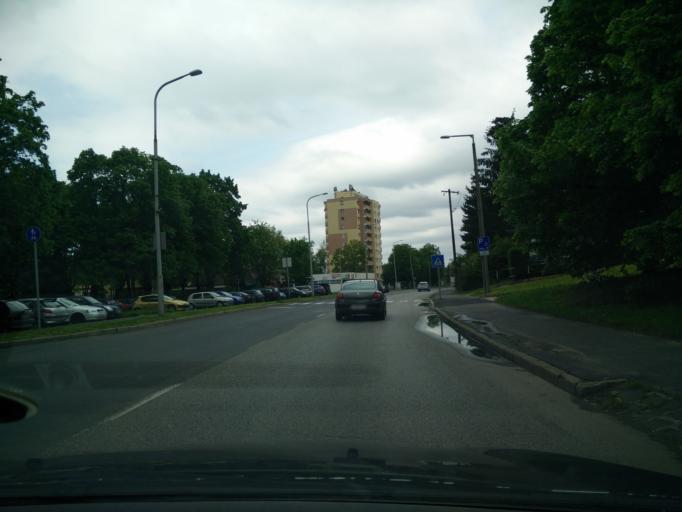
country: HU
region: Zala
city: Zalaegerszeg
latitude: 46.8357
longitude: 16.8314
